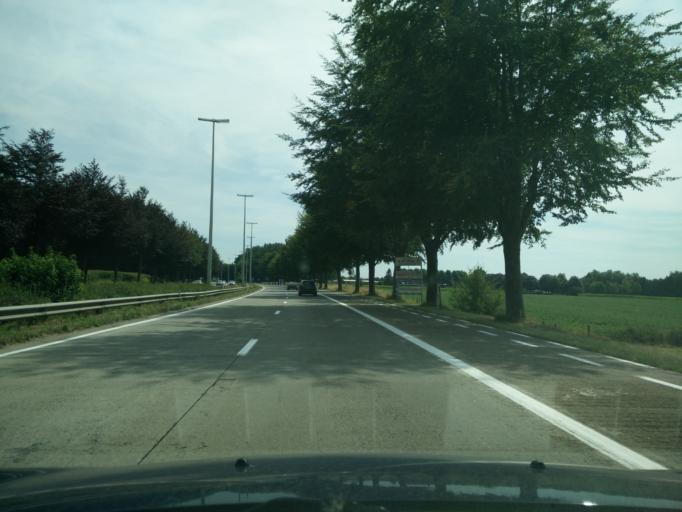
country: BE
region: Flanders
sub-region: Provincie Oost-Vlaanderen
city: Ninove
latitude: 50.8503
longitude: 4.0257
